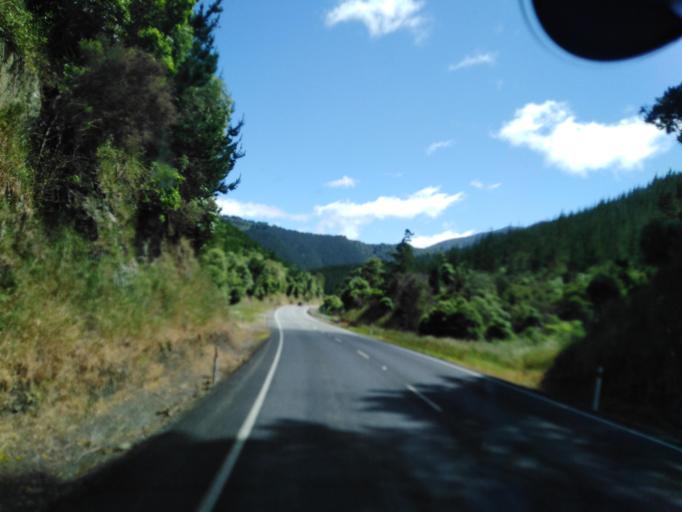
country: NZ
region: Nelson
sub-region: Nelson City
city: Nelson
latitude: -41.1748
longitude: 173.5631
